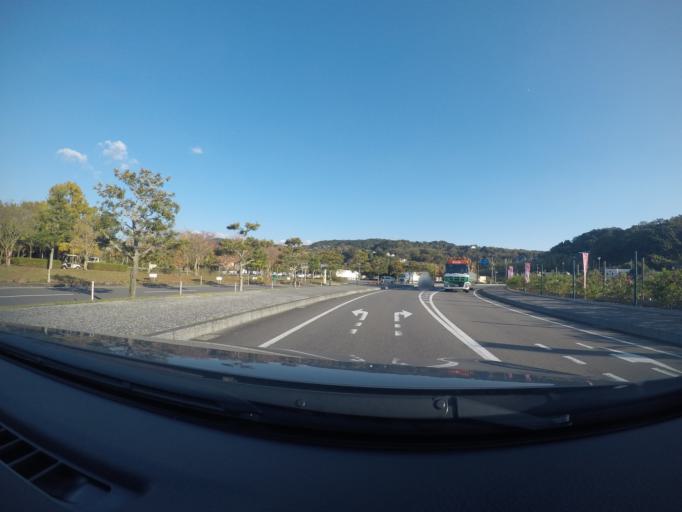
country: JP
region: Kumamoto
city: Minamata
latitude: 32.1998
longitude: 130.3832
